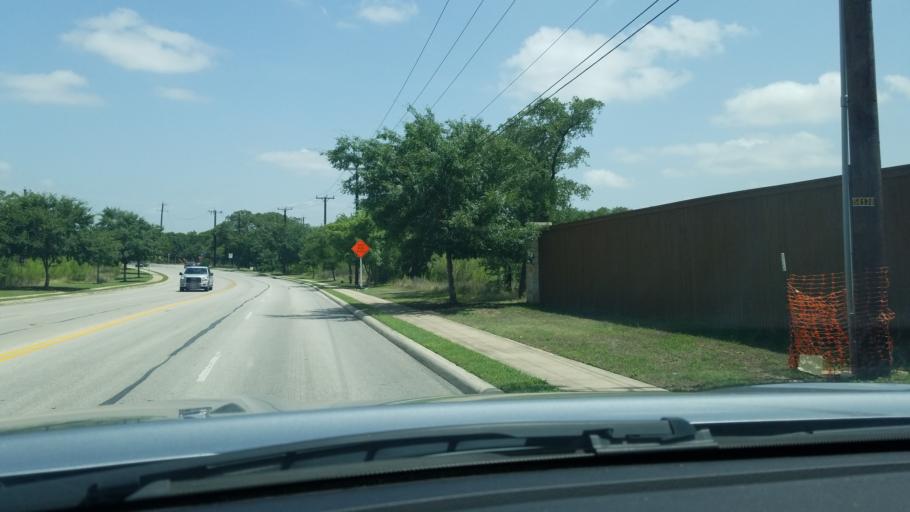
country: US
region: Texas
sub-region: Bexar County
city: Timberwood Park
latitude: 29.7081
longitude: -98.4837
